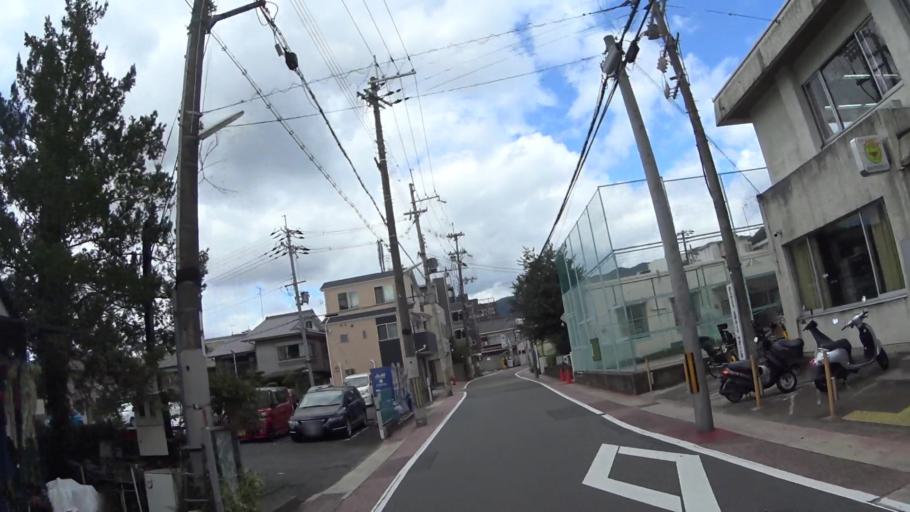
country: JP
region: Shiga Prefecture
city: Otsu-shi
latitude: 34.9859
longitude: 135.8153
